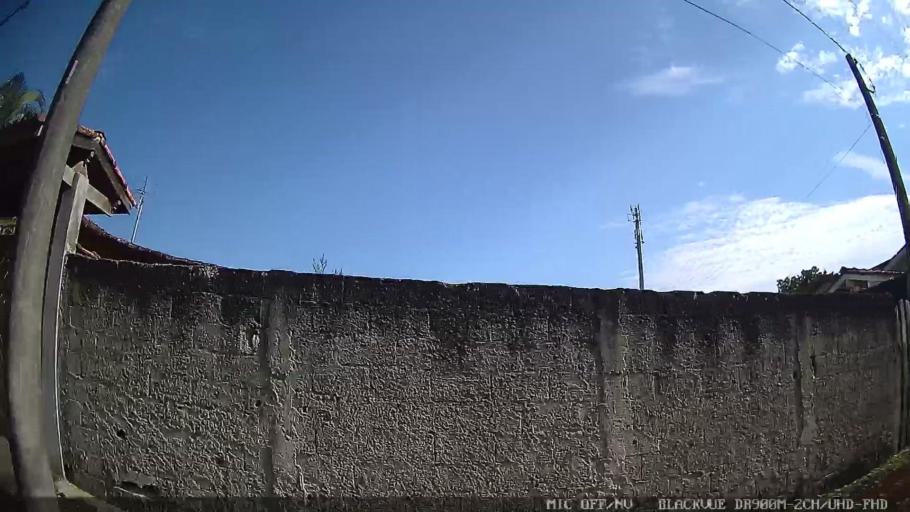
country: BR
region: Sao Paulo
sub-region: Caraguatatuba
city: Caraguatatuba
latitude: -23.6669
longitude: -45.4343
